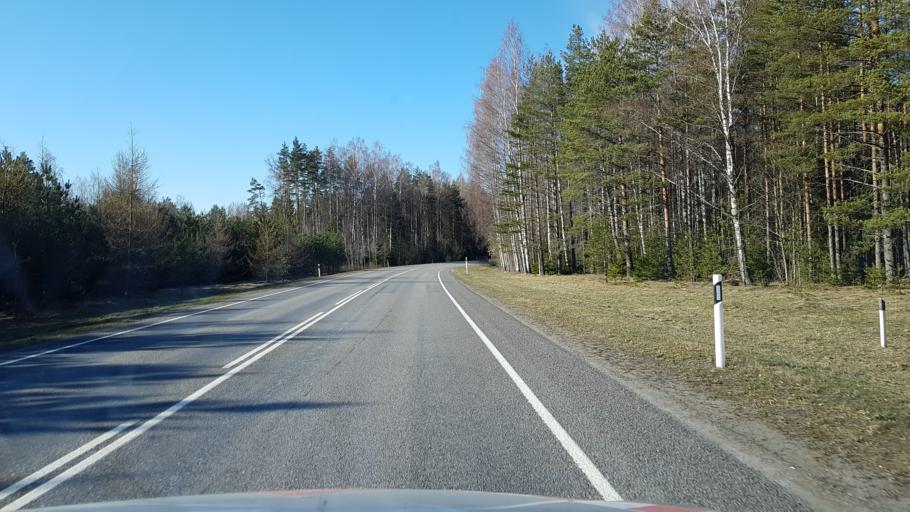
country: EE
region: Jogevamaa
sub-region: Mustvee linn
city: Mustvee
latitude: 59.0082
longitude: 27.2245
